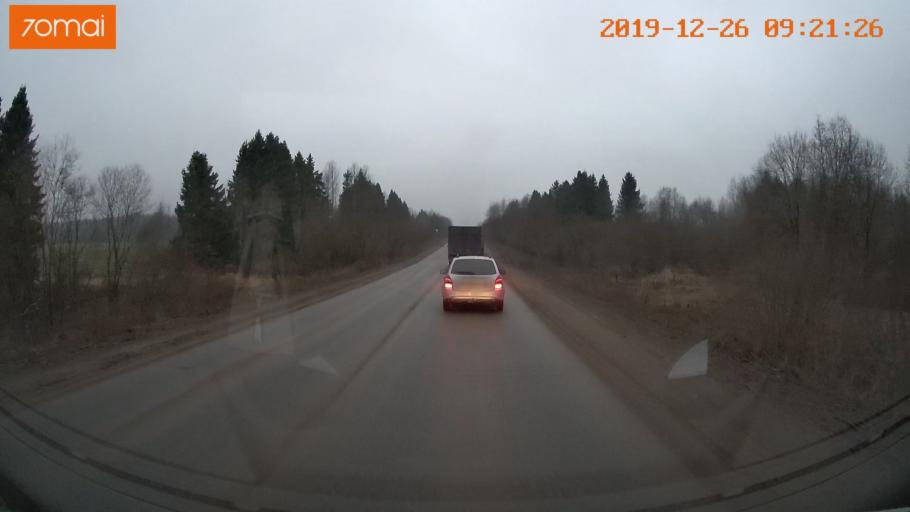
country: RU
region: Vologda
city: Gryazovets
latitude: 58.9703
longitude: 40.2244
